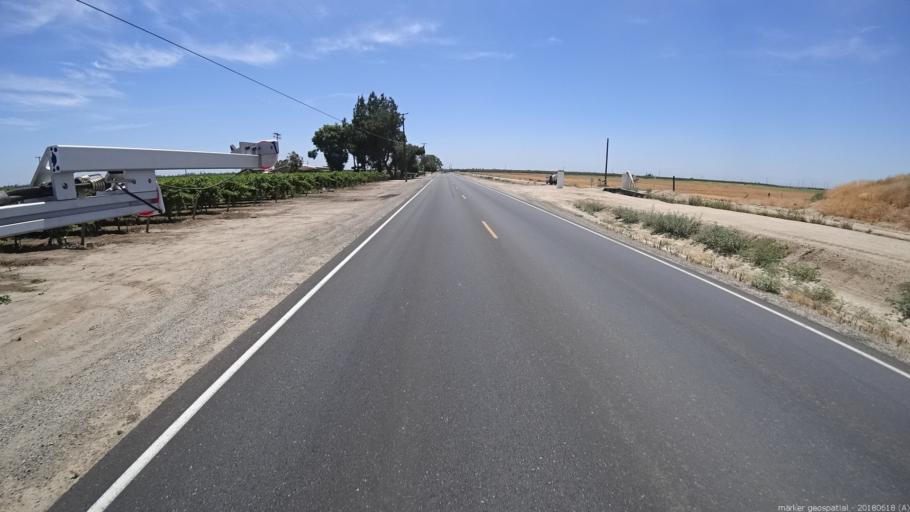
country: US
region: California
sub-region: Madera County
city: Madera
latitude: 36.9300
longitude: -120.0923
